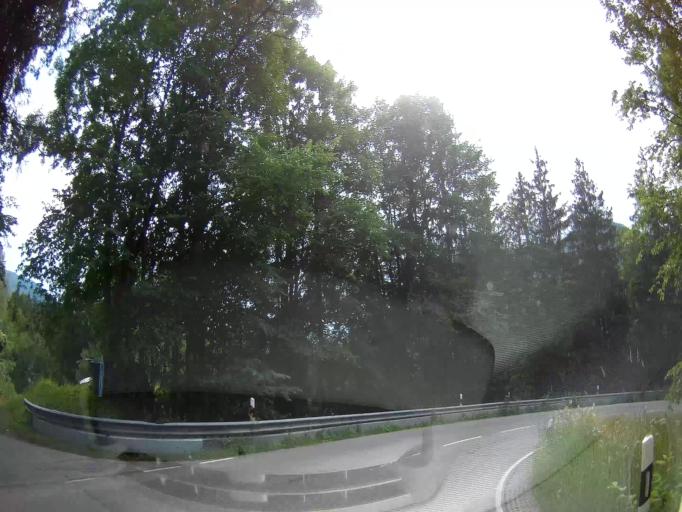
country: DE
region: Bavaria
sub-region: Upper Bavaria
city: Marktschellenberg
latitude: 47.6523
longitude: 13.0506
